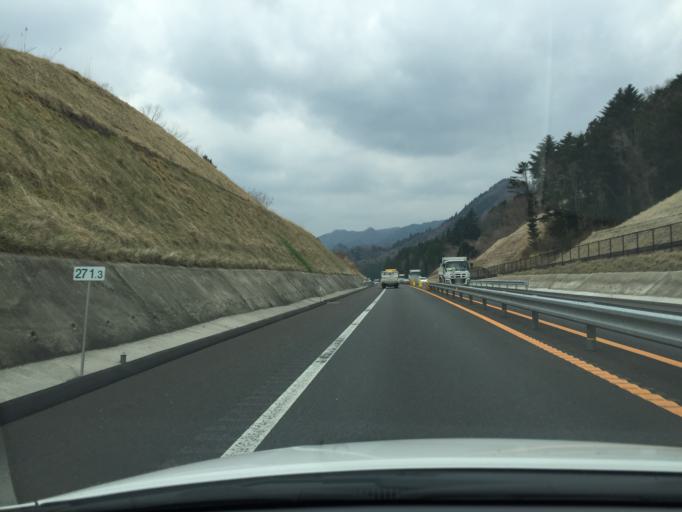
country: JP
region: Miyagi
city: Marumori
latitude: 37.8297
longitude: 140.8766
